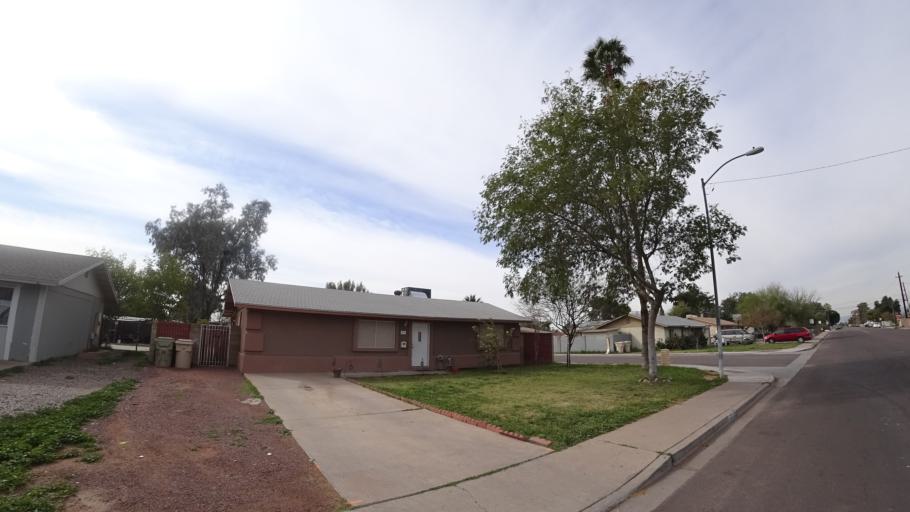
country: US
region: Arizona
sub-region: Maricopa County
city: Glendale
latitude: 33.5348
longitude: -112.1936
